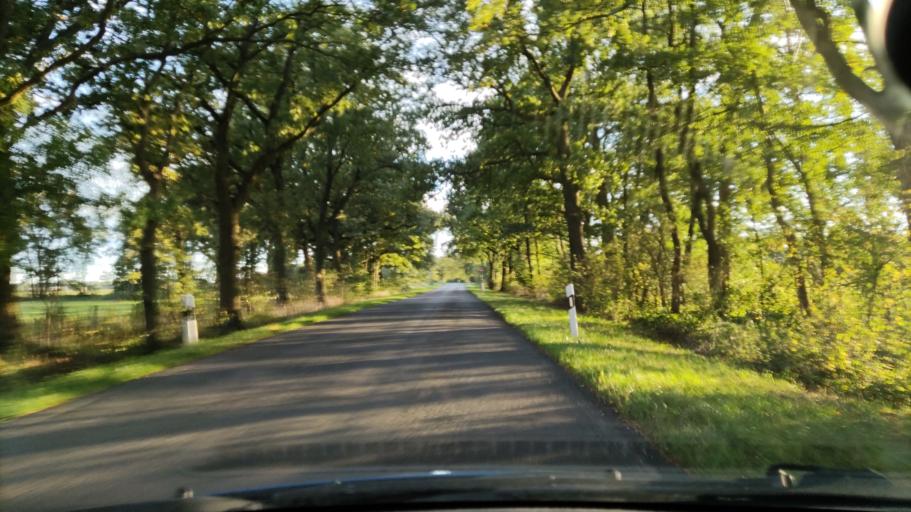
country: DE
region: Lower Saxony
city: Neu Darchau
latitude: 53.3545
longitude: 10.8639
